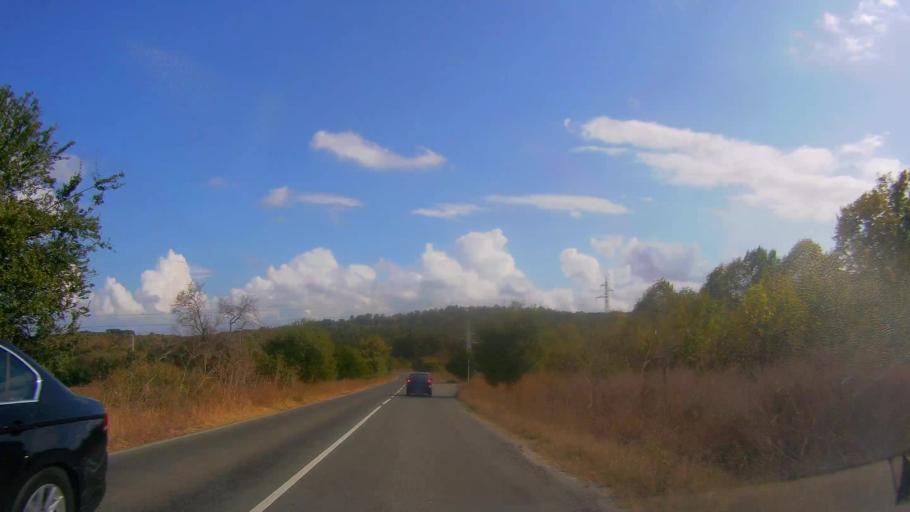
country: BG
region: Burgas
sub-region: Obshtina Burgas
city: Burgas
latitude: 42.4758
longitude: 27.3957
